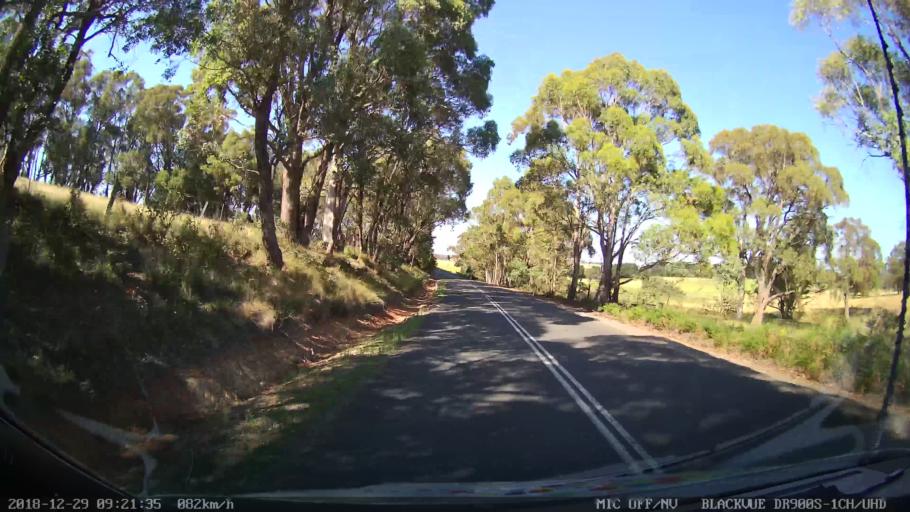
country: AU
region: New South Wales
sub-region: Upper Lachlan Shire
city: Crookwell
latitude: -34.5034
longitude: 149.4130
